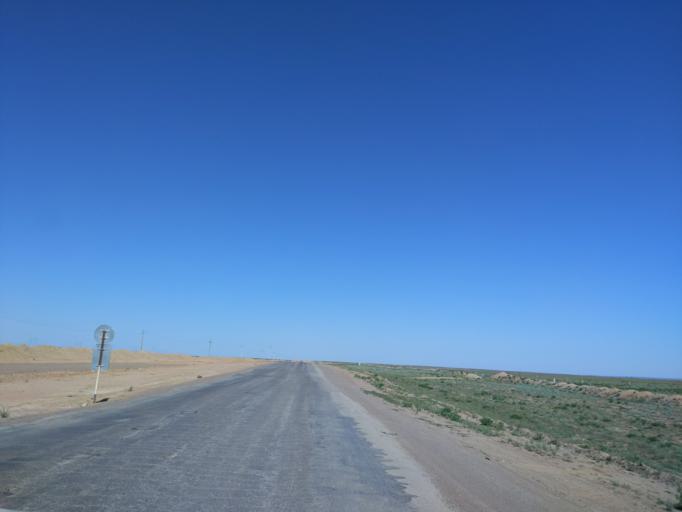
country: KZ
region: Almaty Oblysy
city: Bakanas
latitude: 44.1507
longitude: 75.8629
